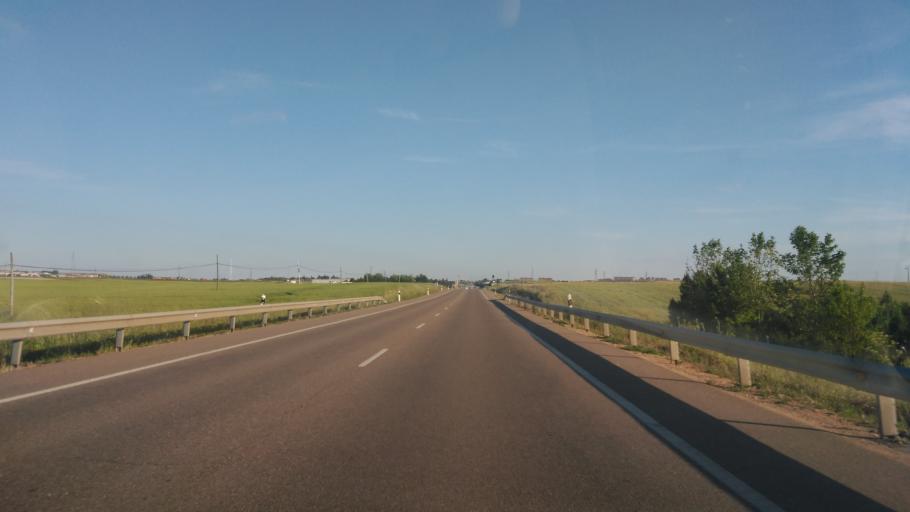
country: ES
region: Castille and Leon
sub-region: Provincia de Salamanca
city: Villares de la Reina
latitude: 41.0127
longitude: -5.6692
